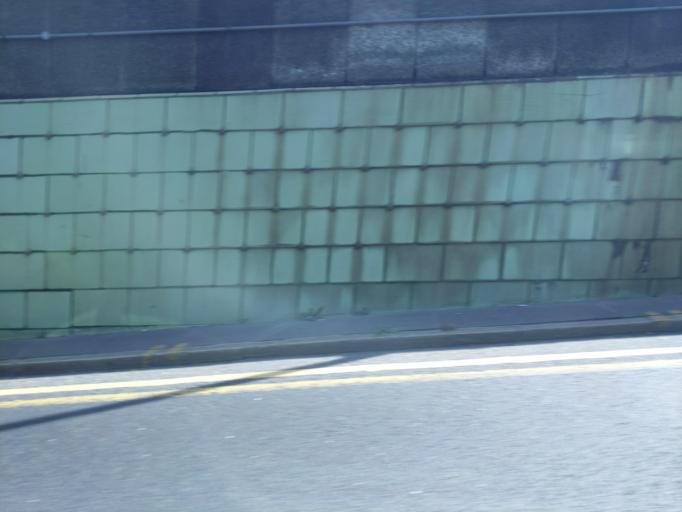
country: GB
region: England
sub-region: Greater London
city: Croydon
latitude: 51.3733
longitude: -0.0965
